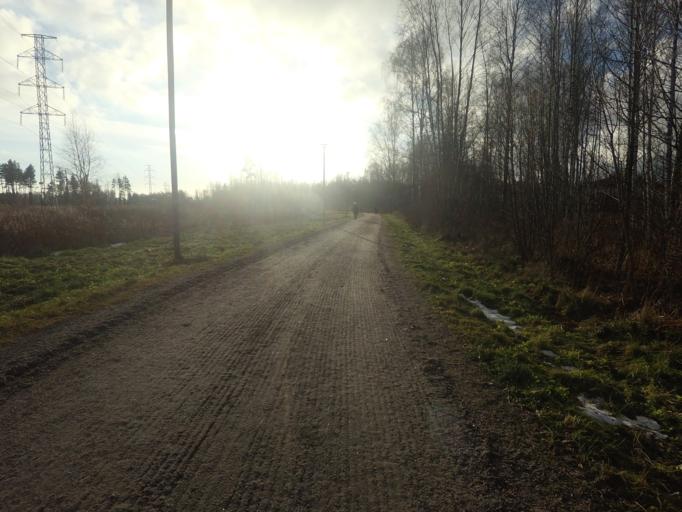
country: FI
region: Uusimaa
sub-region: Helsinki
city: Kilo
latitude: 60.2007
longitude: 24.7742
